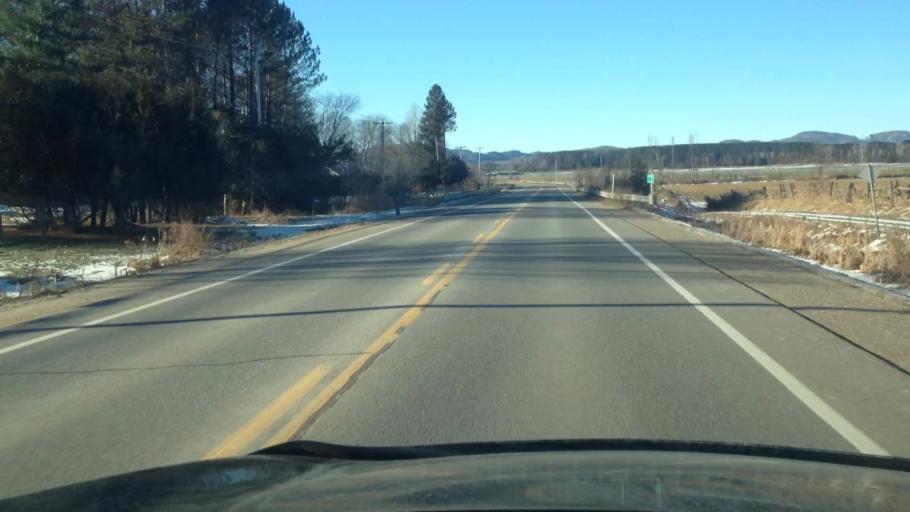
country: CA
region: Quebec
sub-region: Laurentides
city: Mont-Tremblant
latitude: 45.9612
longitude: -74.5819
